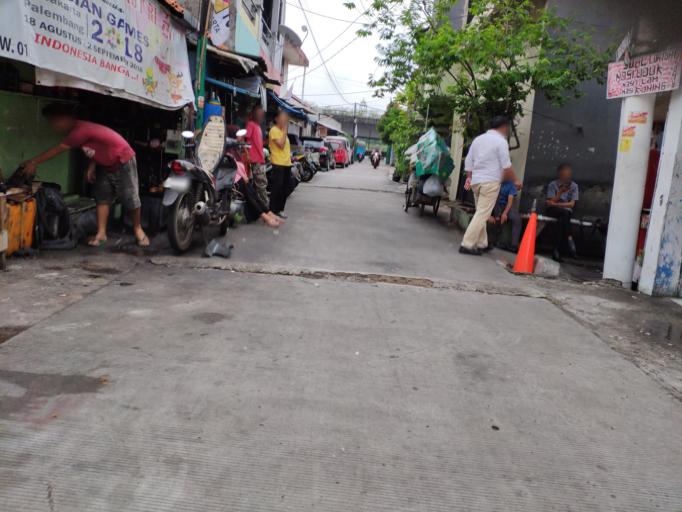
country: ID
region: Jakarta Raya
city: Jakarta
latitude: -6.1992
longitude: 106.8552
